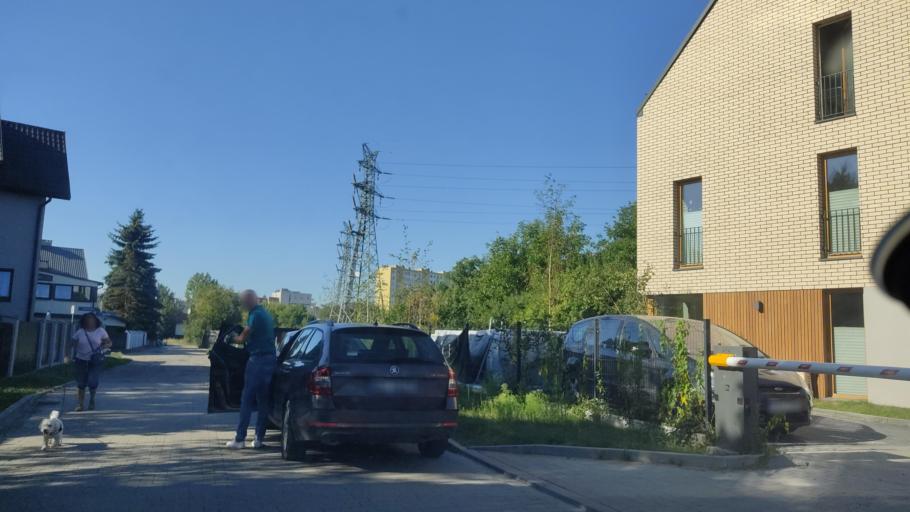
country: PL
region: Lesser Poland Voivodeship
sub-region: Powiat krakowski
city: Zielonki
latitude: 50.0969
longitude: 19.9288
